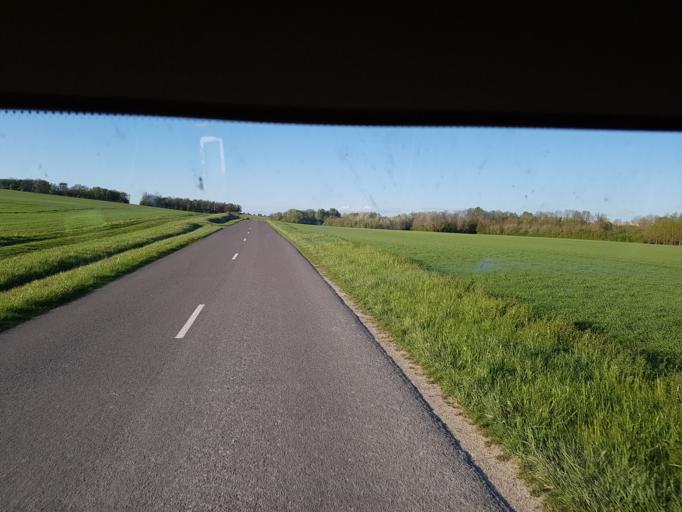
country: FR
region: Champagne-Ardenne
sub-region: Departement de l'Aube
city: Marigny-le-Chatel
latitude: 48.4198
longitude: 3.6681
